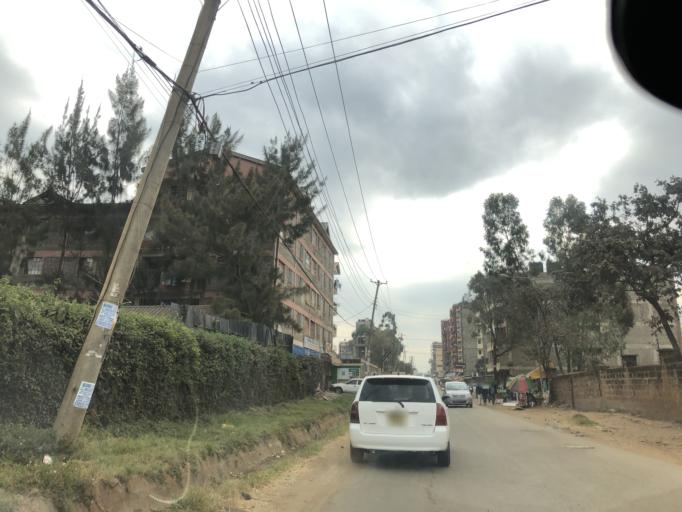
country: KE
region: Kiambu
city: Kiambu
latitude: -1.2114
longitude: 36.8881
